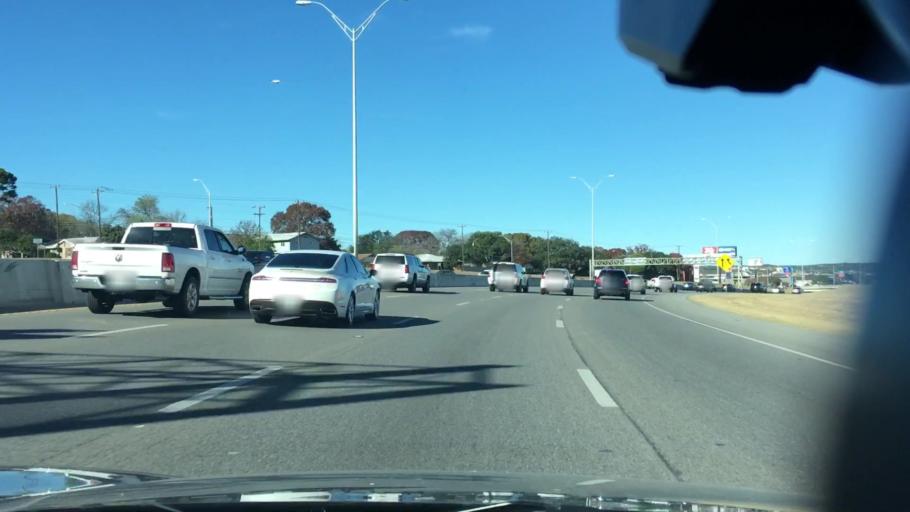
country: US
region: Texas
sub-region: Bexar County
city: Castle Hills
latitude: 29.5381
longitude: -98.4926
